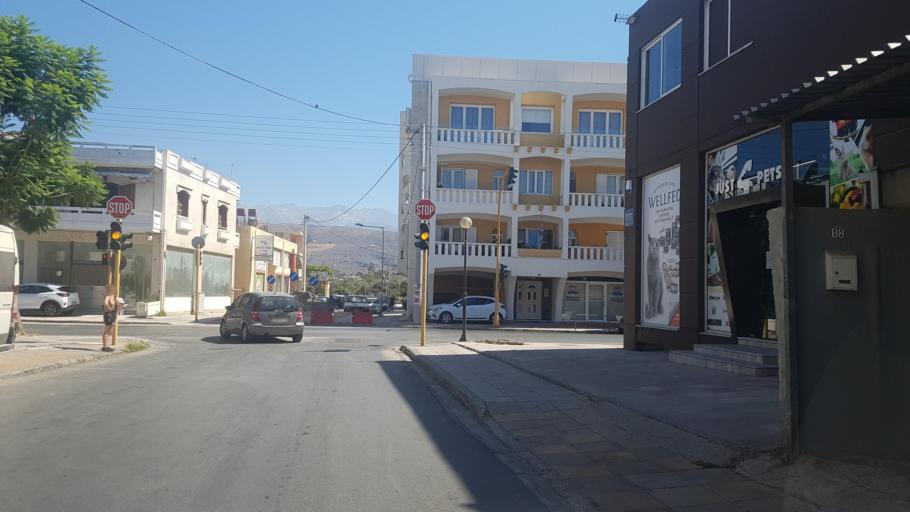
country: GR
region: Crete
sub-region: Nomos Chanias
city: Chania
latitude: 35.5045
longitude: 24.0178
